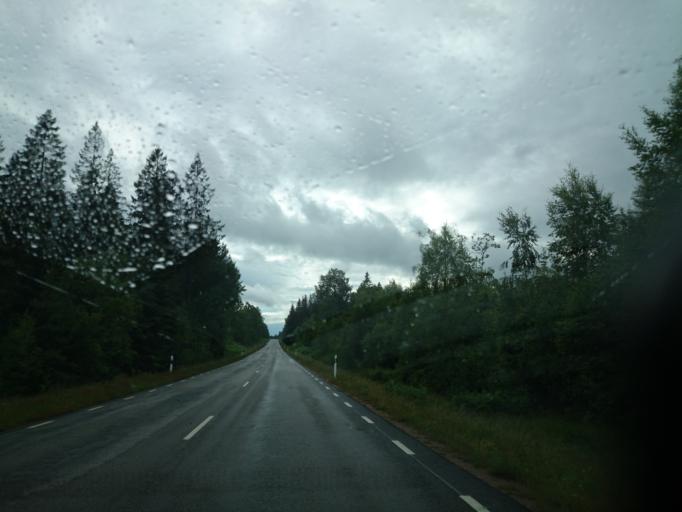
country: SE
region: Joenkoeping
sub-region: Varnamo Kommun
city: Varnamo
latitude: 57.1107
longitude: 13.9647
